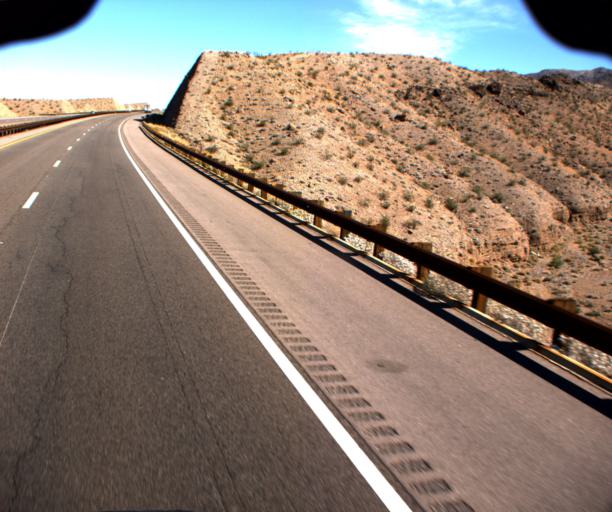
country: US
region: Nevada
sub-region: Clark County
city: Boulder City
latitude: 35.8951
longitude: -114.6252
